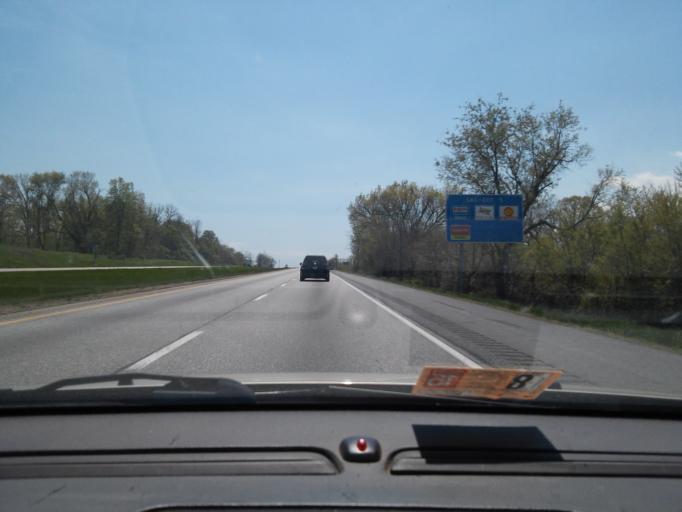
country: US
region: Pennsylvania
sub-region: Franklin County
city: Greencastle
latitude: 39.7963
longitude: -77.7107
